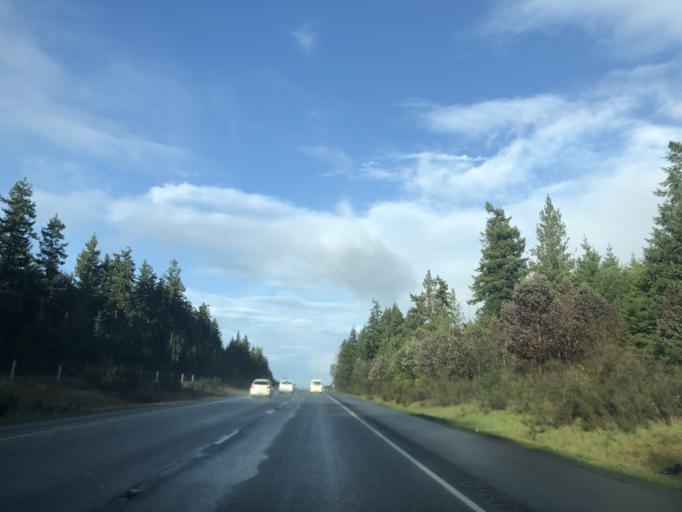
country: US
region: Washington
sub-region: Kitsap County
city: Poulsbo
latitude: 47.7211
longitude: -122.6786
